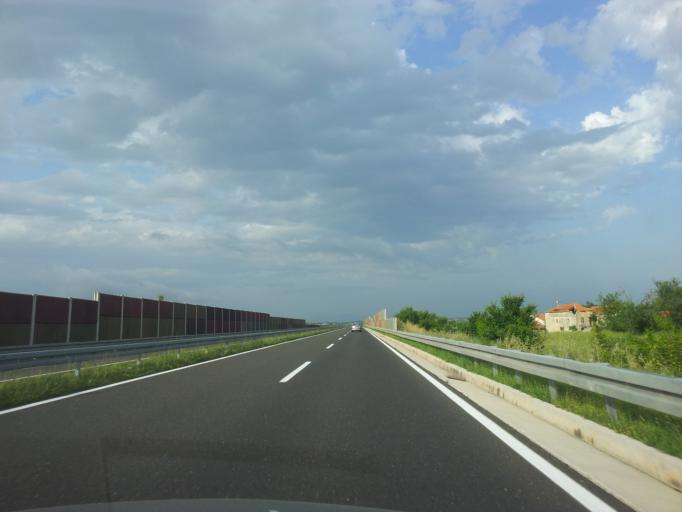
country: HR
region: Zadarska
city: Galovac
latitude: 44.0994
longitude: 15.3841
